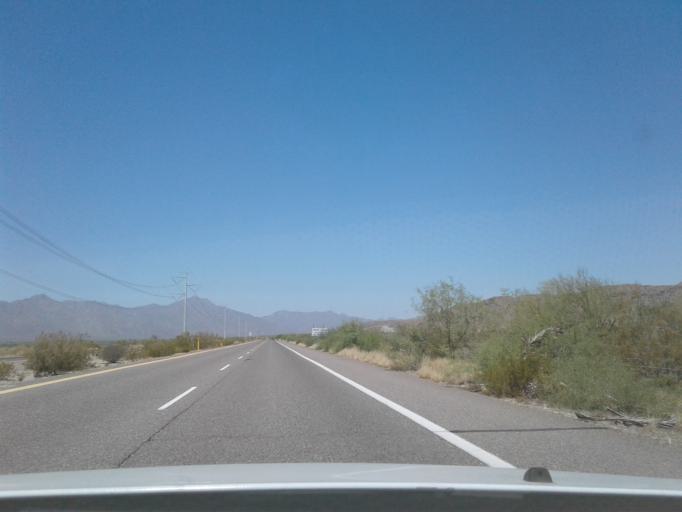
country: US
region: Arizona
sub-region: Maricopa County
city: Laveen
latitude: 33.2911
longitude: -112.1045
